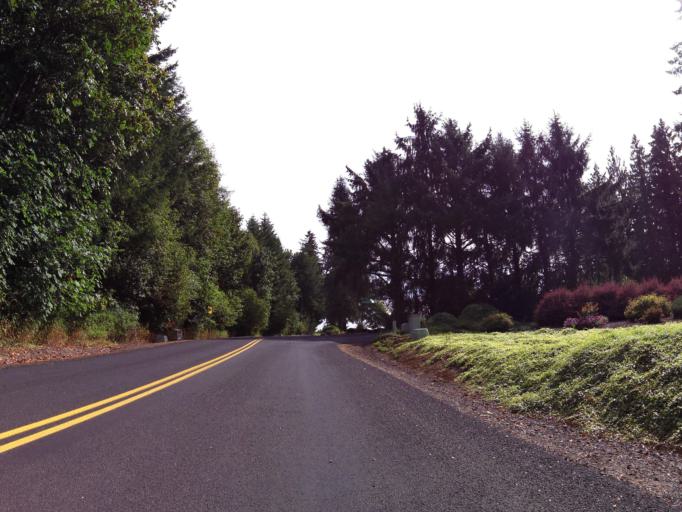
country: US
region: Washington
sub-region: Cowlitz County
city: Castle Rock
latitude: 46.3139
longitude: -122.9246
